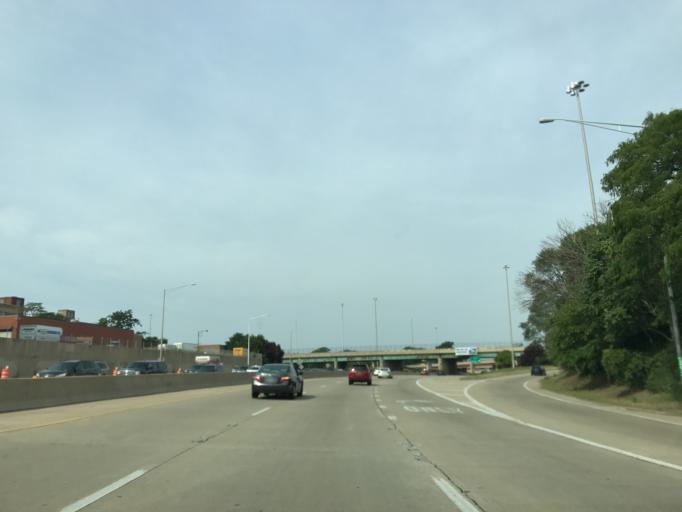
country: US
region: Illinois
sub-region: Cook County
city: Chicago
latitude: 41.8472
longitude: -87.6274
